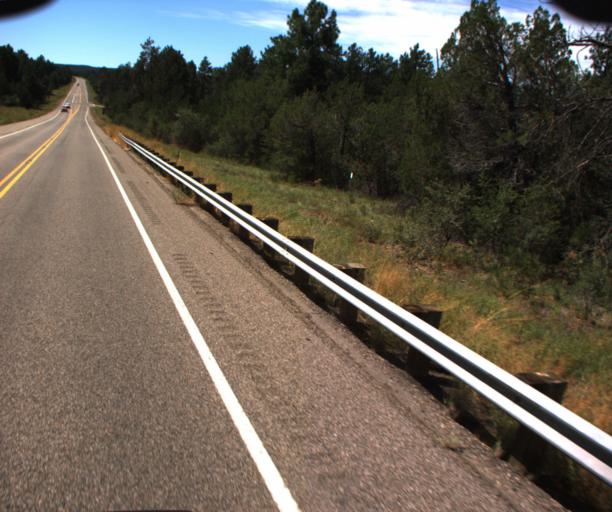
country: US
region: Arizona
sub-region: Navajo County
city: Cibecue
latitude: 33.6904
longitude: -110.5698
